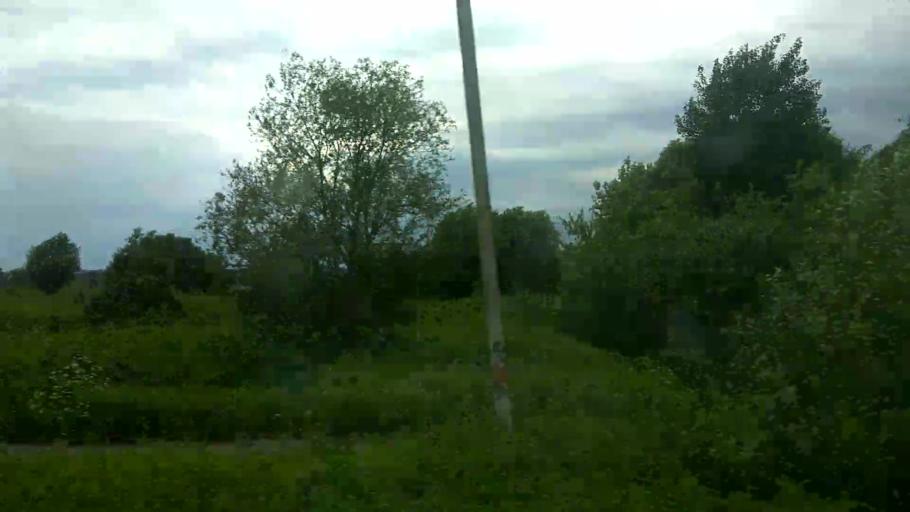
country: RU
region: Moskovskaya
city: Ozery
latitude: 54.8463
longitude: 38.5661
